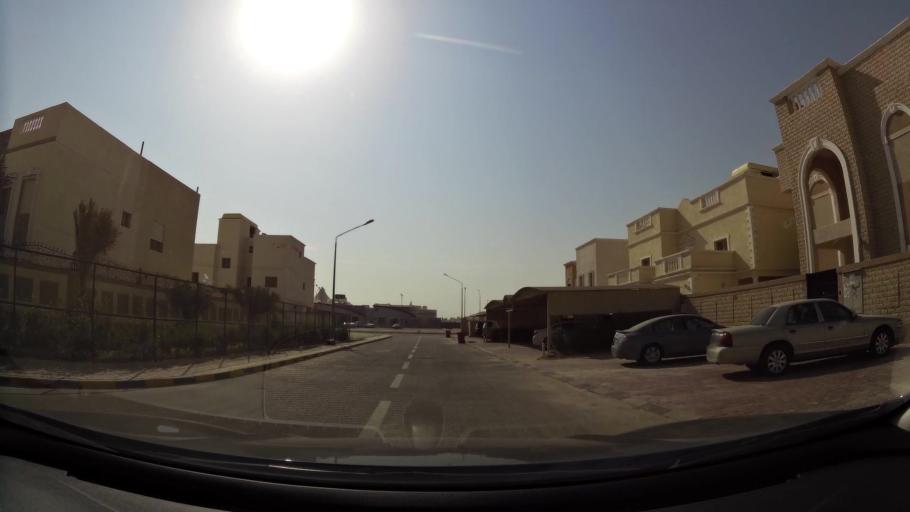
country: KW
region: Al Ahmadi
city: Al Wafrah
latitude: 28.7948
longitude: 48.0685
